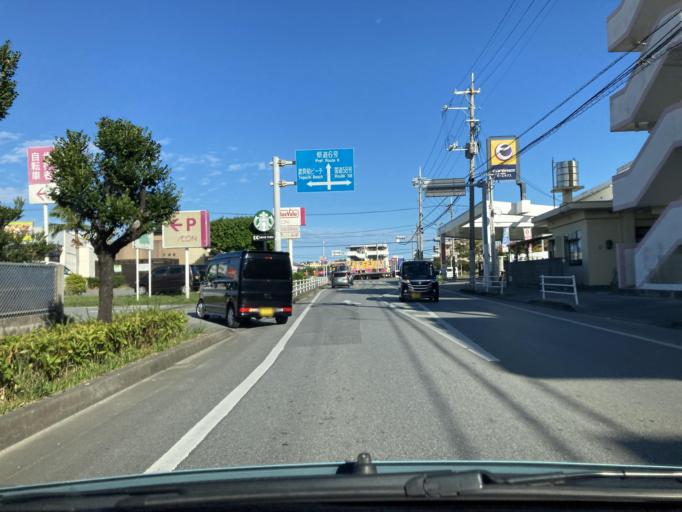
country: JP
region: Okinawa
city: Okinawa
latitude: 26.3692
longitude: 127.7469
